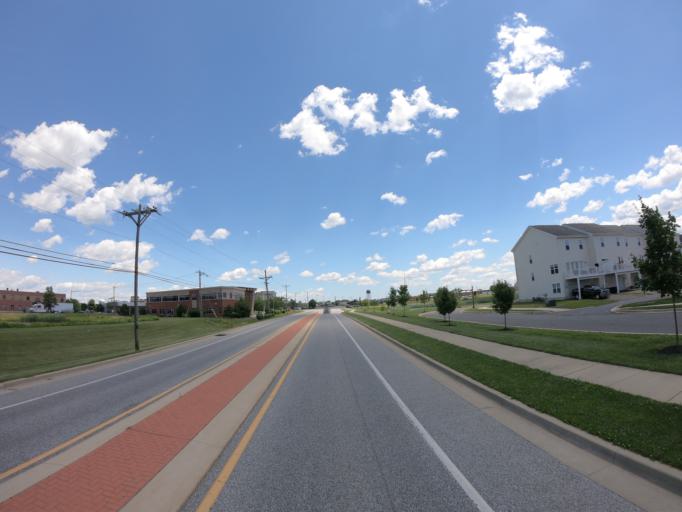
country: US
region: Delaware
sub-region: New Castle County
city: Middletown
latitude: 39.4517
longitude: -75.7332
